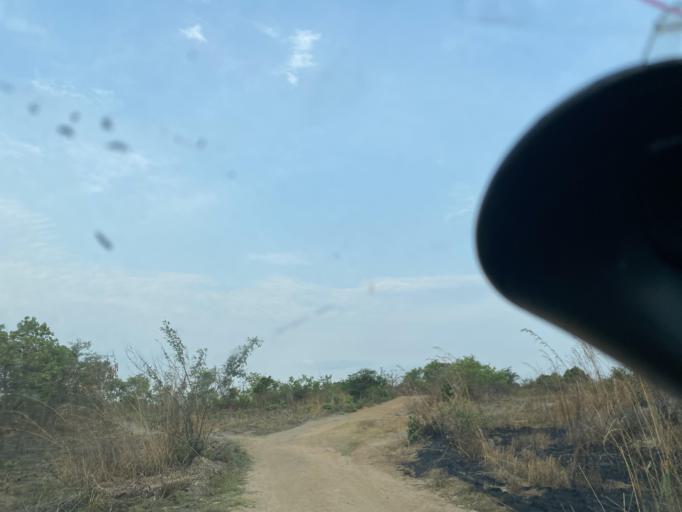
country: ZM
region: Lusaka
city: Chongwe
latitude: -15.2079
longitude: 28.5051
